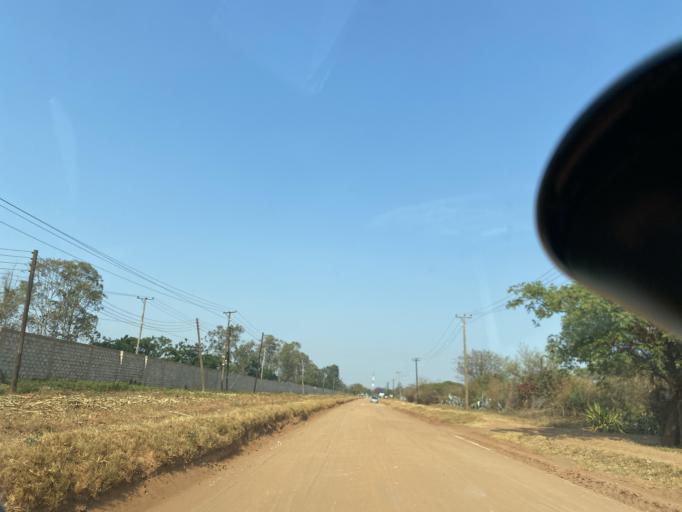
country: ZM
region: Lusaka
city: Lusaka
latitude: -15.4819
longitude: 28.1720
